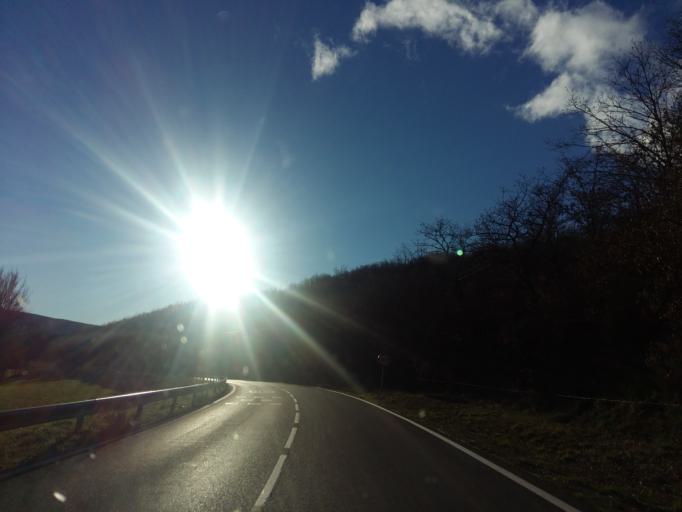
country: ES
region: Cantabria
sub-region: Provincia de Cantabria
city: San Martin de Elines
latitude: 42.8171
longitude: -3.9239
